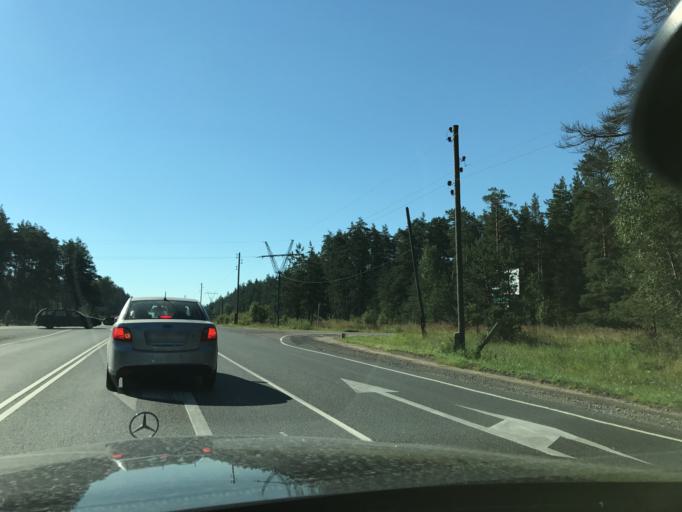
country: RU
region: Moskovskaya
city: Noginsk-9
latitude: 56.0942
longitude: 38.6741
